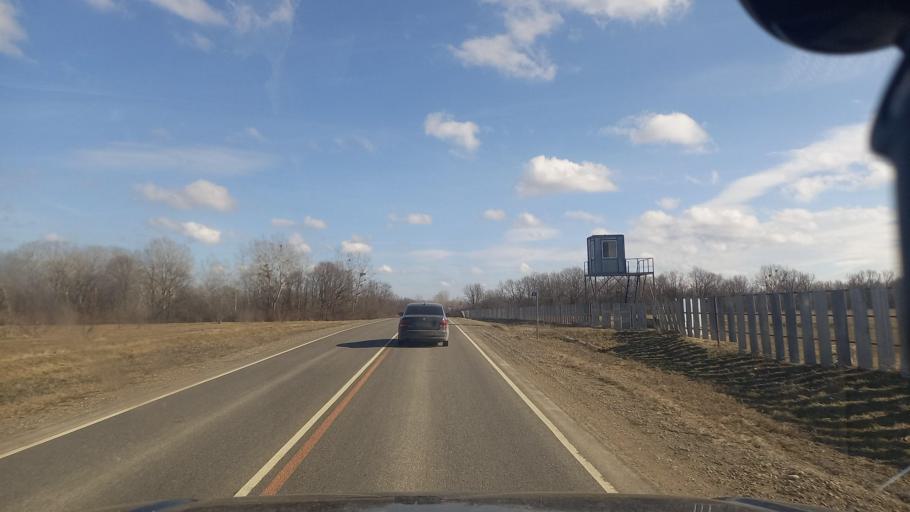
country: RU
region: Krasnodarskiy
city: Novodmitriyevskaya
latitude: 44.7874
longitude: 38.9558
